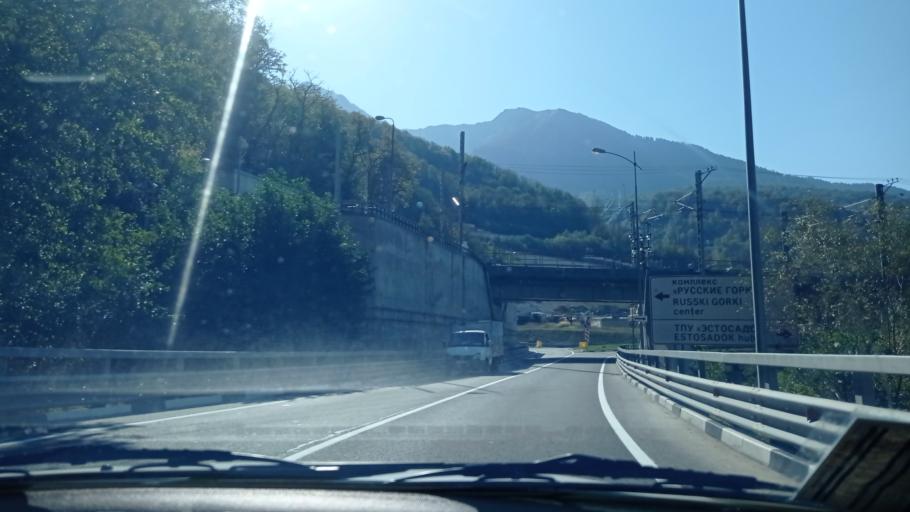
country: RU
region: Krasnodarskiy
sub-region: Sochi City
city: Krasnaya Polyana
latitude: 43.6849
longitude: 40.2457
